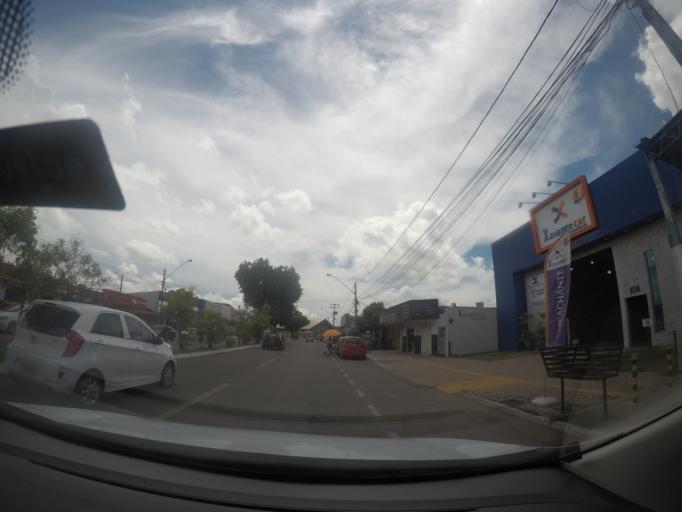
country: BR
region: Goias
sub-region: Goiania
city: Goiania
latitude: -16.6796
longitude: -49.3097
